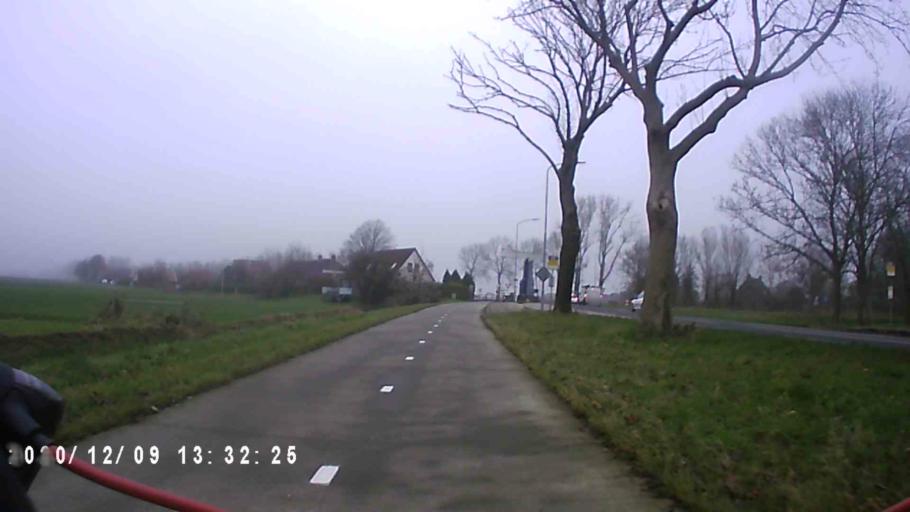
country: NL
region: Groningen
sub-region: Gemeente Bedum
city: Bedum
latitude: 53.2773
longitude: 6.6009
